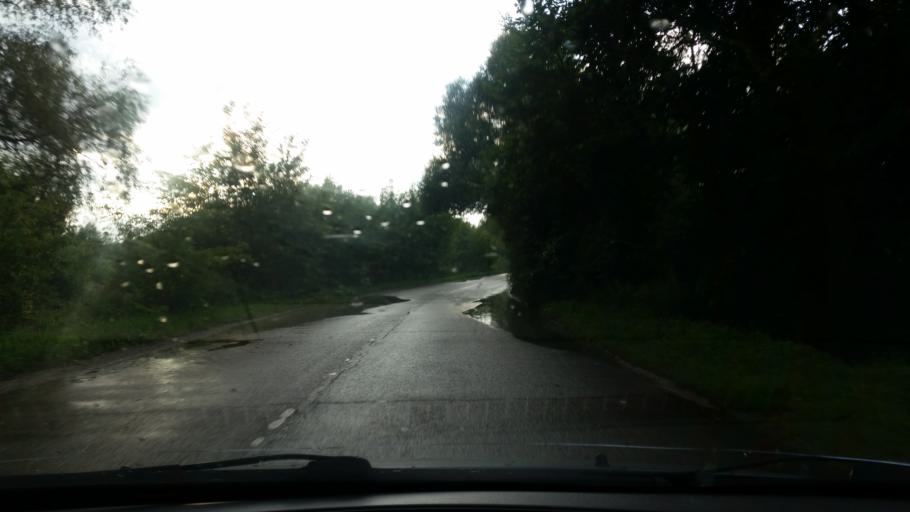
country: RU
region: Moskovskaya
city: Bol'shoye Gryzlovo
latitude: 54.8751
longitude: 37.8233
